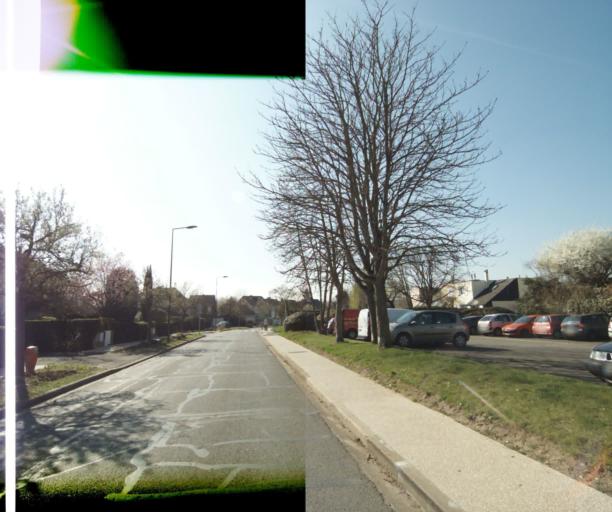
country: FR
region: Ile-de-France
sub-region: Departement du Val-d'Oise
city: Cergy
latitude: 49.0369
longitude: 2.0668
